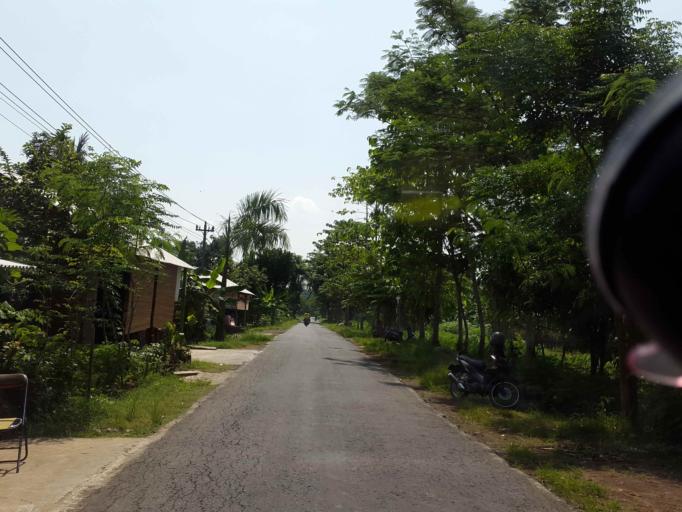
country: ID
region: Central Java
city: Pemalang
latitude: -6.9479
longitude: 109.3783
